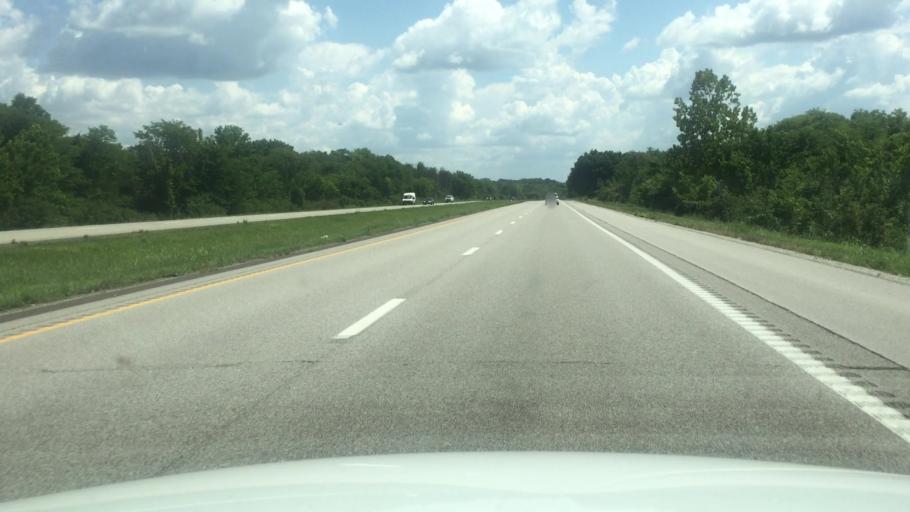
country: US
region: Missouri
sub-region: Platte County
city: Weatherby Lake
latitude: 39.2623
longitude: -94.7578
